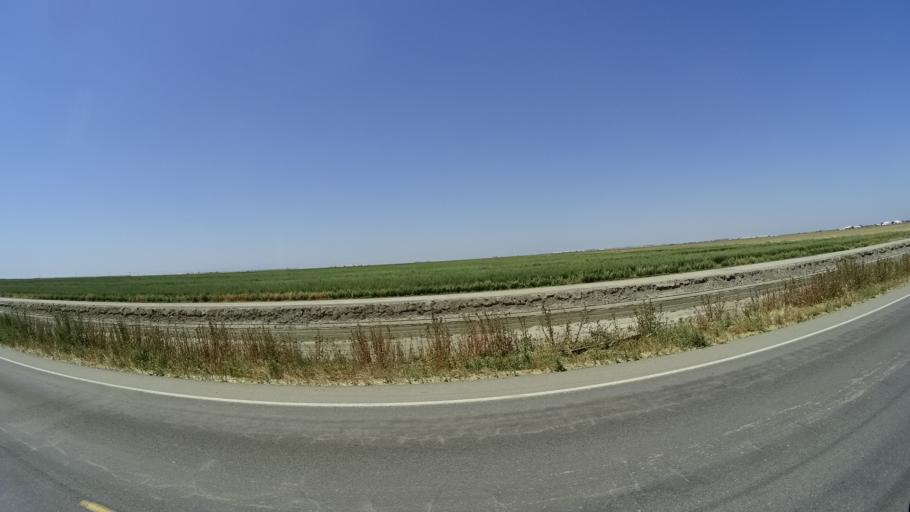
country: US
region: California
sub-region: Kings County
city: Corcoran
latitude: 36.1736
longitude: -119.6464
